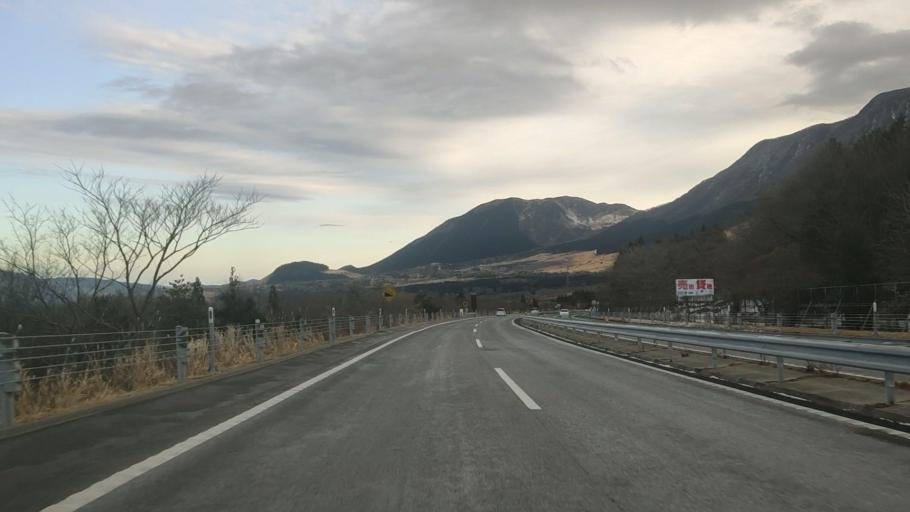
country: JP
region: Oita
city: Beppu
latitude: 33.2991
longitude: 131.3820
